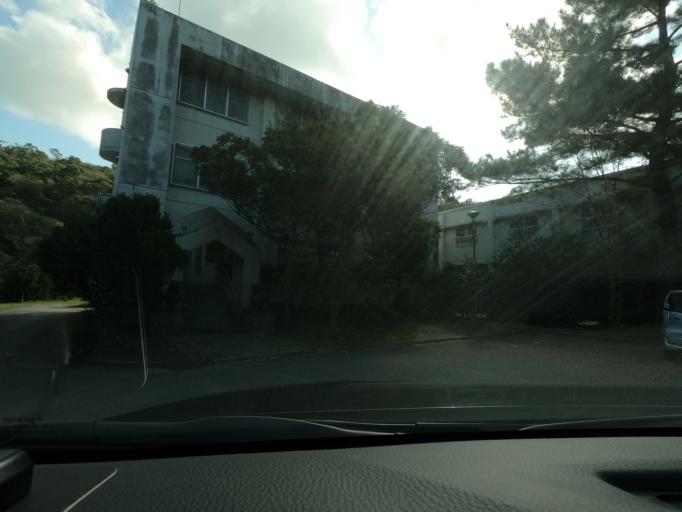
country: JP
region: Okinawa
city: Nago
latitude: 26.7631
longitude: 128.2158
